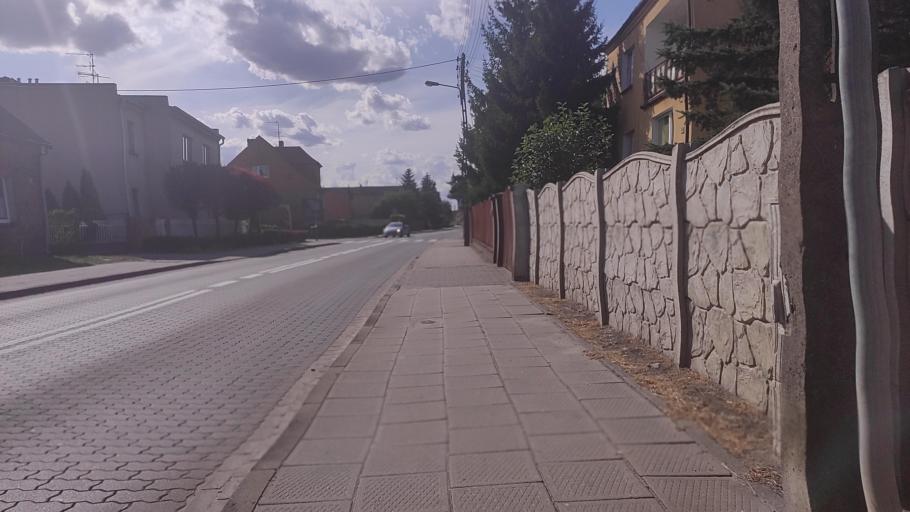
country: PL
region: Greater Poland Voivodeship
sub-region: Powiat poznanski
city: Swarzedz
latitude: 52.4021
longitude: 17.0779
